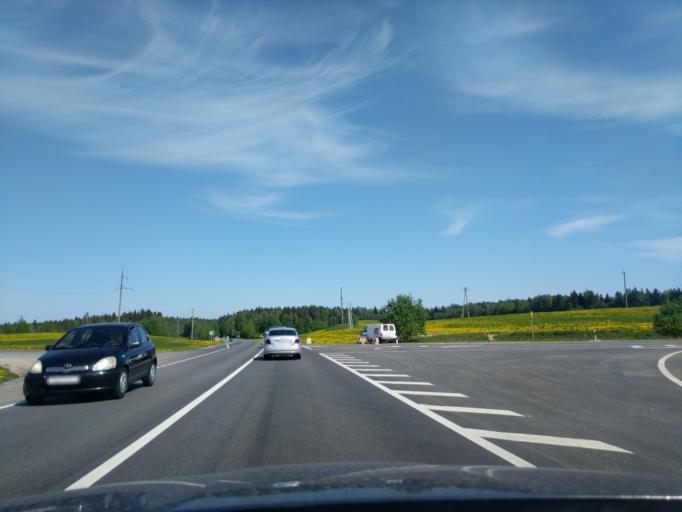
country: BY
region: Minsk
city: Bal'shavik
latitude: 54.0988
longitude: 27.5346
